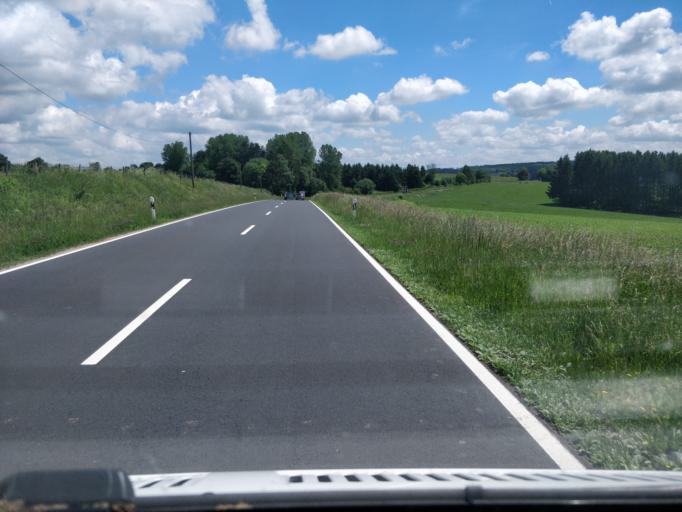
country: DE
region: Rheinland-Pfalz
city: Scheid
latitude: 50.3558
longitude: 6.4091
